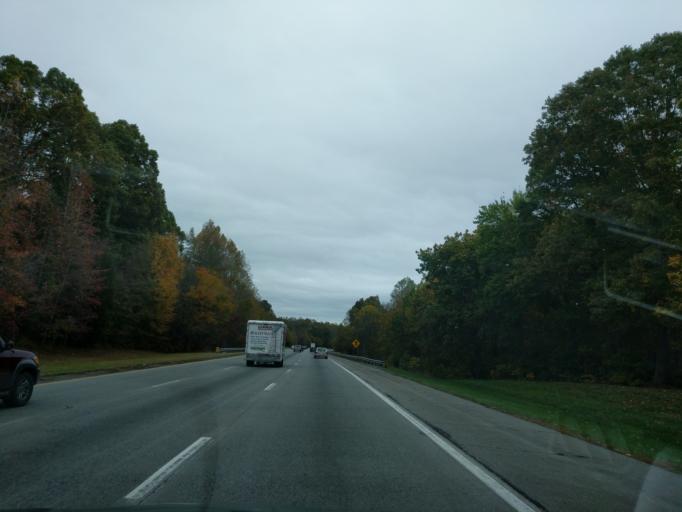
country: US
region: North Carolina
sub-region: Davidson County
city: Thomasville
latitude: 35.8408
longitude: -80.1358
